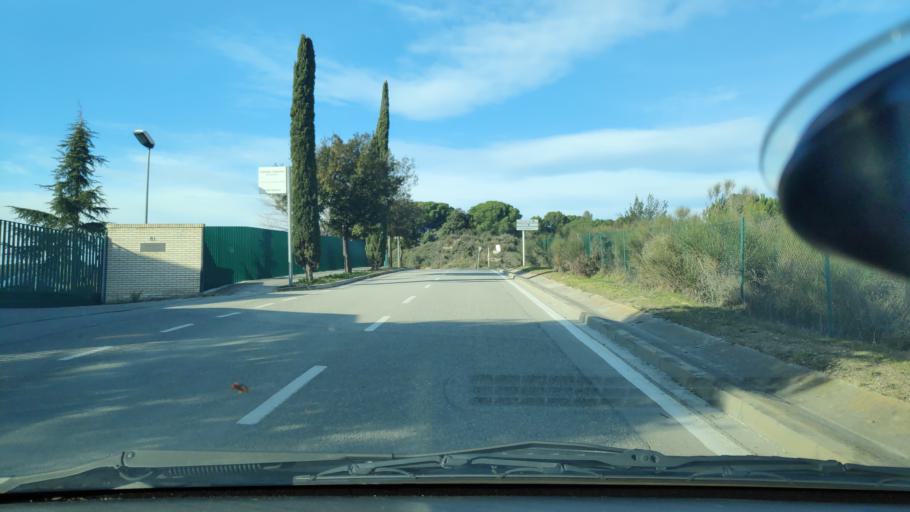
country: ES
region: Catalonia
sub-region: Provincia de Barcelona
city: Rubi
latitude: 41.4968
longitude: 2.0643
